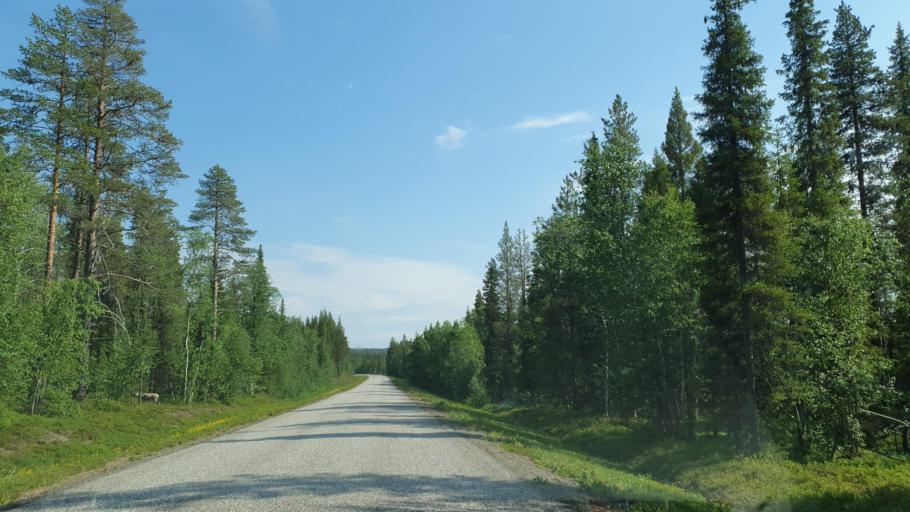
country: FI
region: Lapland
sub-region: Tunturi-Lappi
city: Muonio
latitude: 67.9261
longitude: 24.1402
